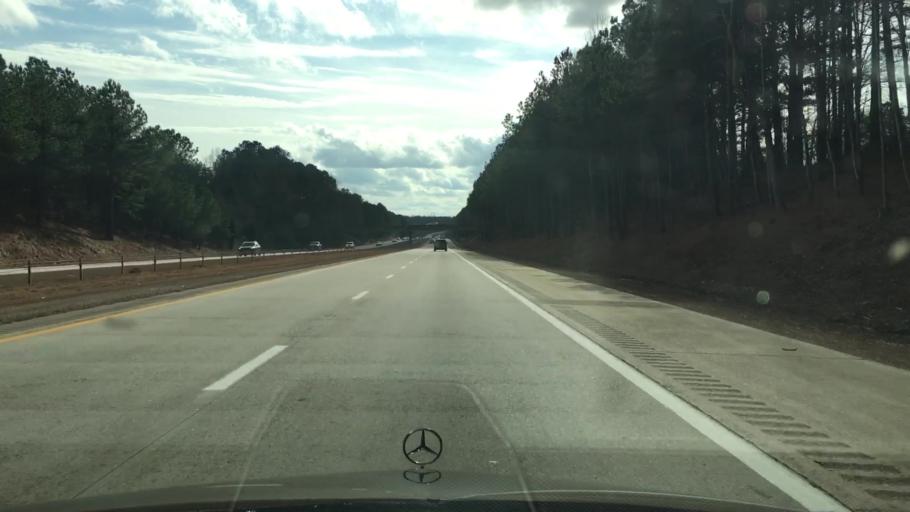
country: US
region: North Carolina
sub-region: Wake County
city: Garner
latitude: 35.5771
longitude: -78.5766
